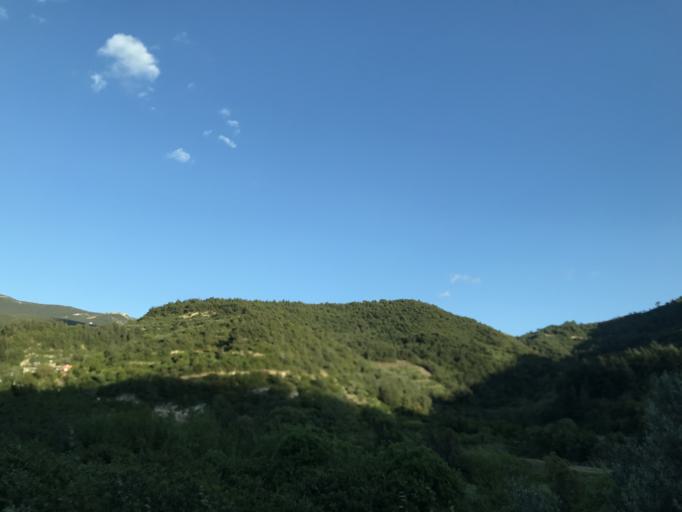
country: TR
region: Hatay
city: Buyukcat
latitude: 36.0910
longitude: 36.0609
